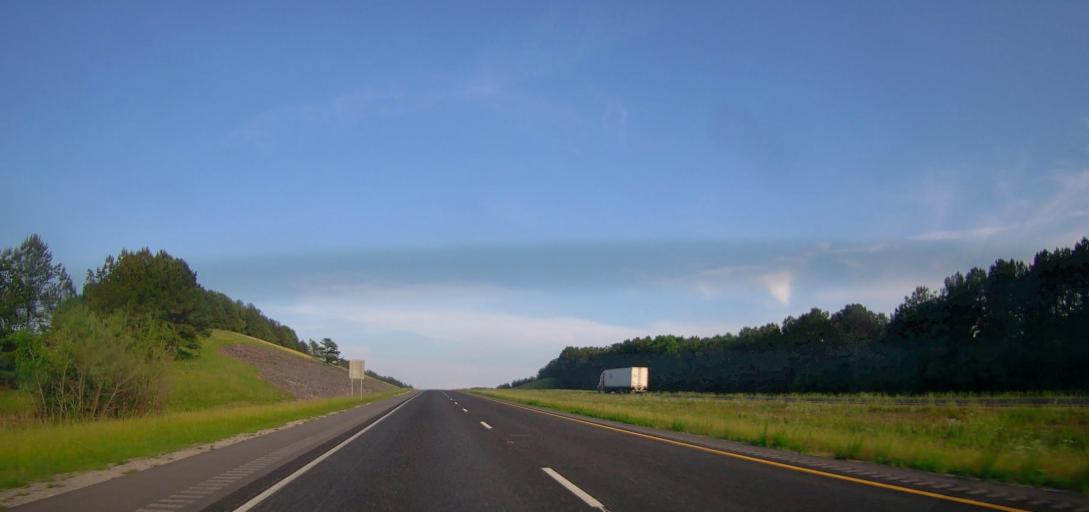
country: US
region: Alabama
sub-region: Marion County
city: Hamilton
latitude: 34.0588
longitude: -87.9471
